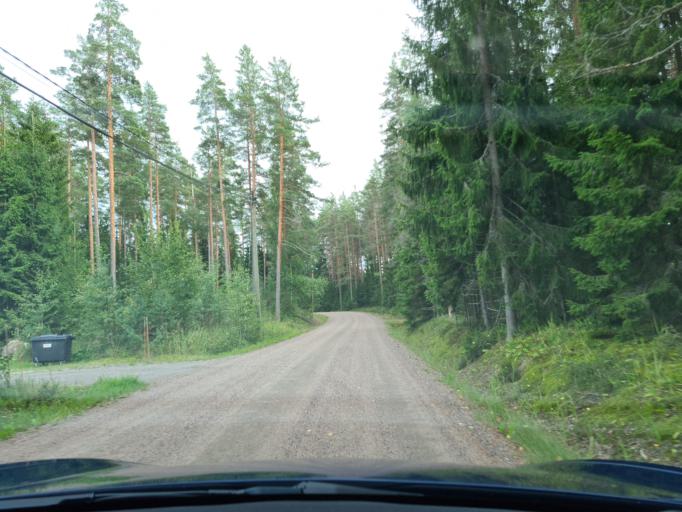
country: FI
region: Uusimaa
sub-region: Helsinki
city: Vihti
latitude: 60.4212
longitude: 24.4776
